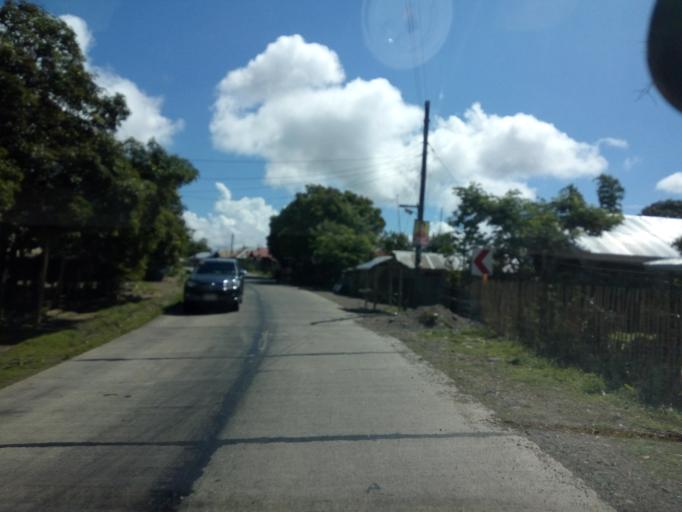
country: PH
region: Central Luzon
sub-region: Province of Nueva Ecija
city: General Luna
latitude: 15.7716
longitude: 121.2060
